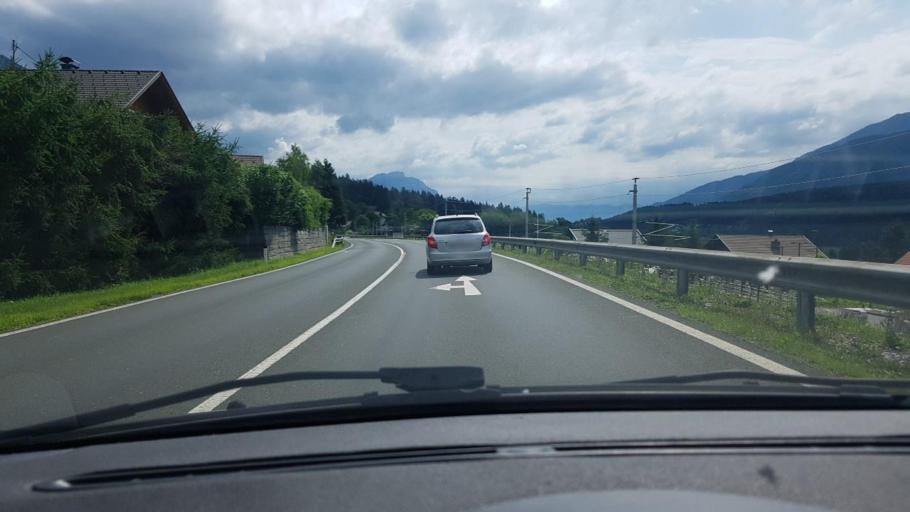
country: AT
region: Carinthia
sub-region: Politischer Bezirk Hermagor
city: Hermagor
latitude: 46.6315
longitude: 13.4080
